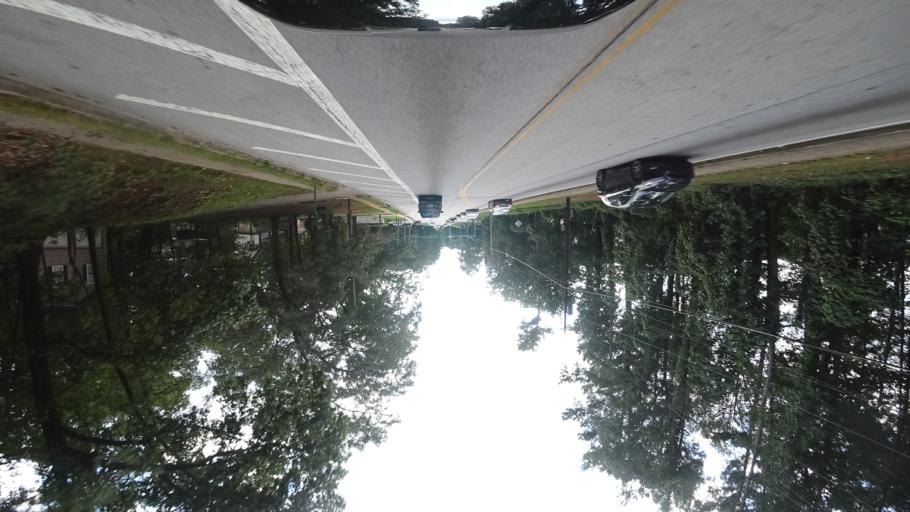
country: US
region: Georgia
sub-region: DeKalb County
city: Redan
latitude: 33.7599
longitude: -84.1766
